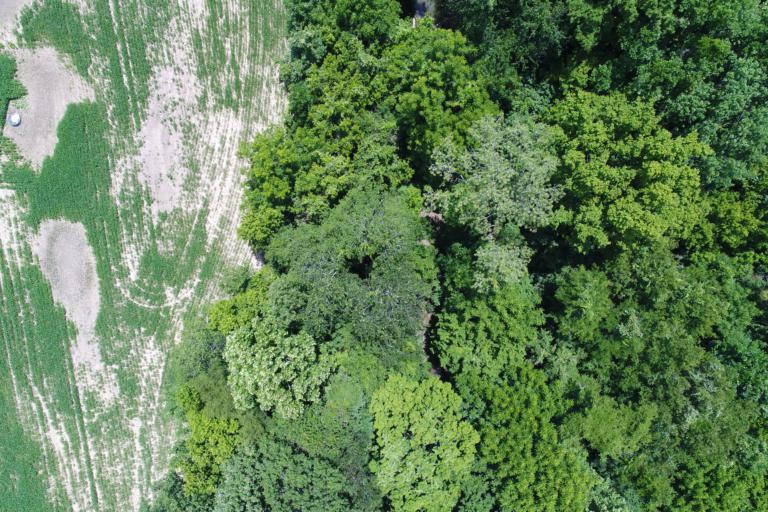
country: US
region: Mississippi
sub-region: De Soto County
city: Walls
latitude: 34.9275
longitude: -90.1347
